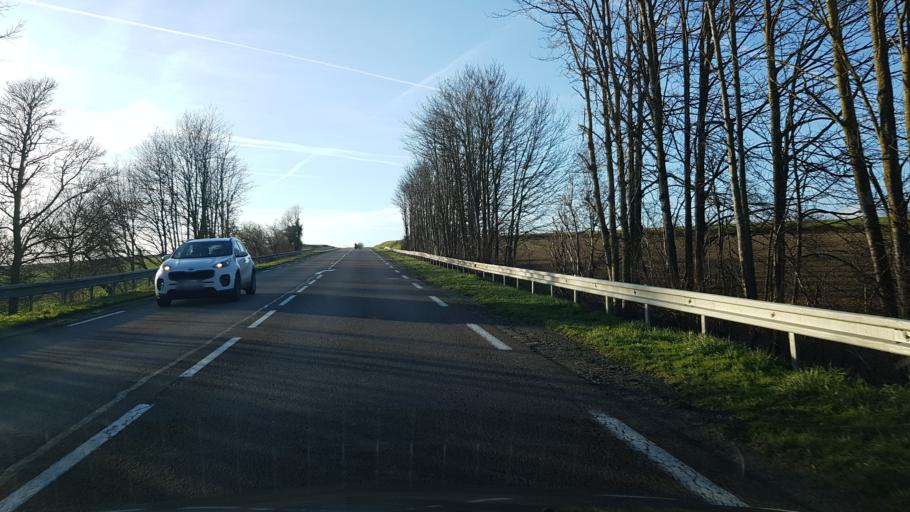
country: FR
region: Champagne-Ardenne
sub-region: Departement de l'Aube
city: Mailly-le-Camp
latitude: 48.7346
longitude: 4.2914
